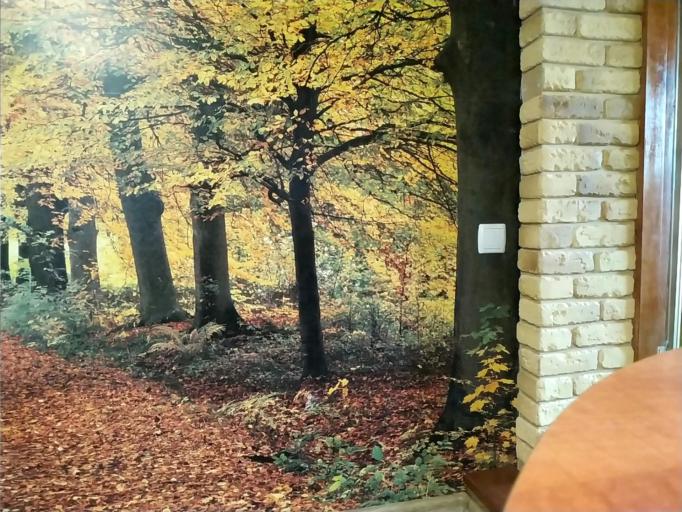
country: RU
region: Leningrad
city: Tolmachevo
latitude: 58.9367
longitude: 29.6913
